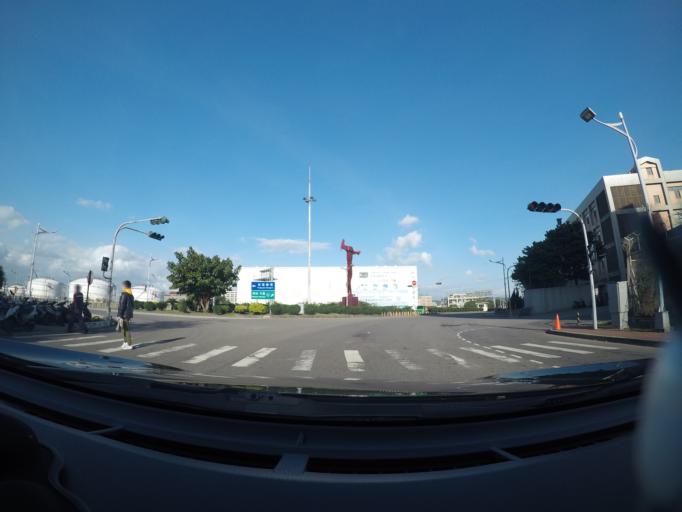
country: TW
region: Taiwan
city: Taoyuan City
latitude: 25.0892
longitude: 121.2499
